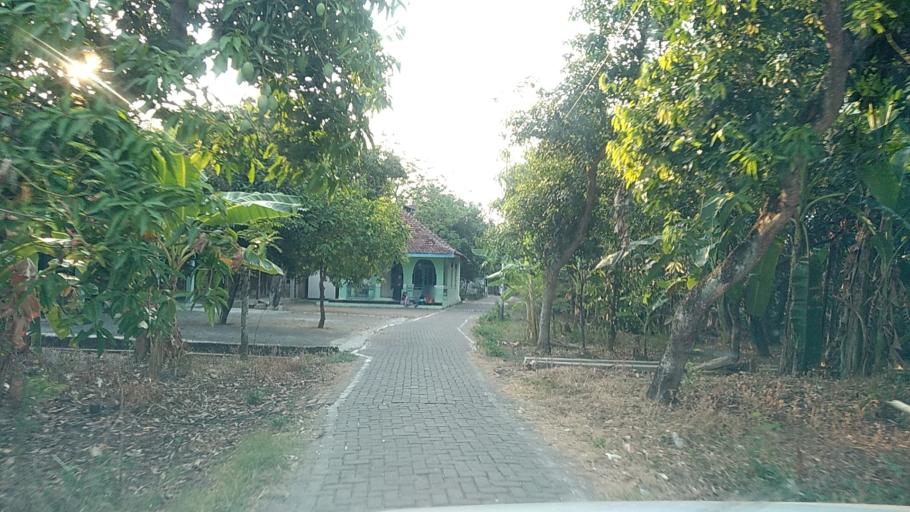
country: ID
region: Central Java
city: Semarang
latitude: -6.9680
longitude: 110.2925
